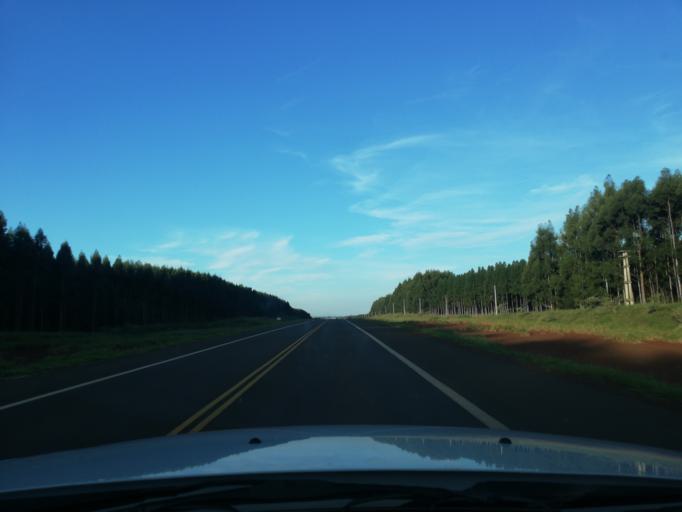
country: AR
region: Misiones
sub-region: Departamento de Capital
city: Posadas
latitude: -27.4653
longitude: -55.9530
